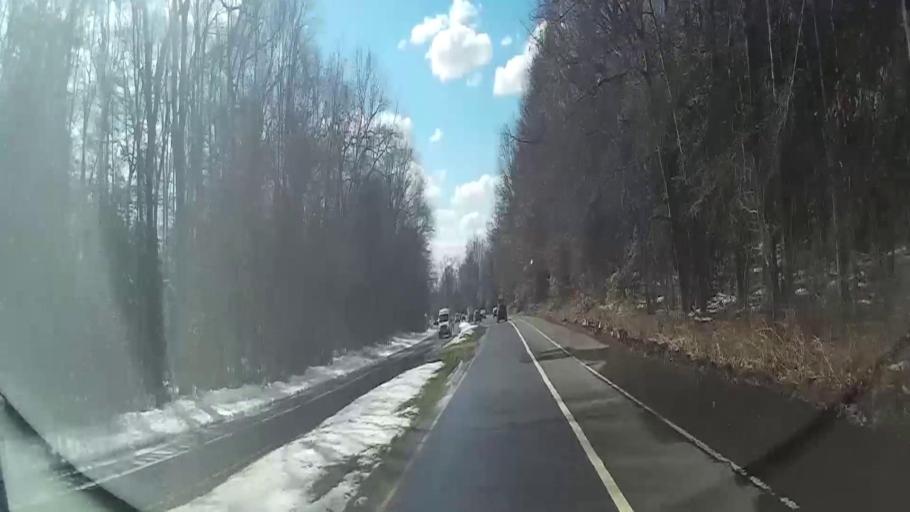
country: US
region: New Jersey
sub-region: Burlington County
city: Marlton
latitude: 39.8754
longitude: -74.9167
